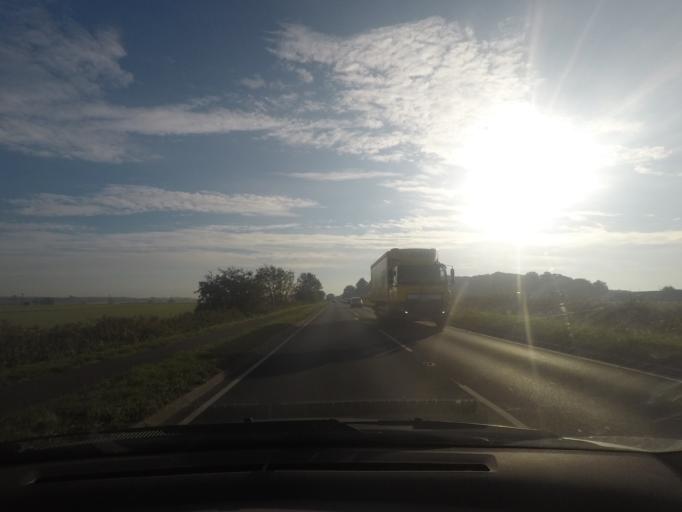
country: GB
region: England
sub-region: East Riding of Yorkshire
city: Londesborough
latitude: 53.8725
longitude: -0.6956
